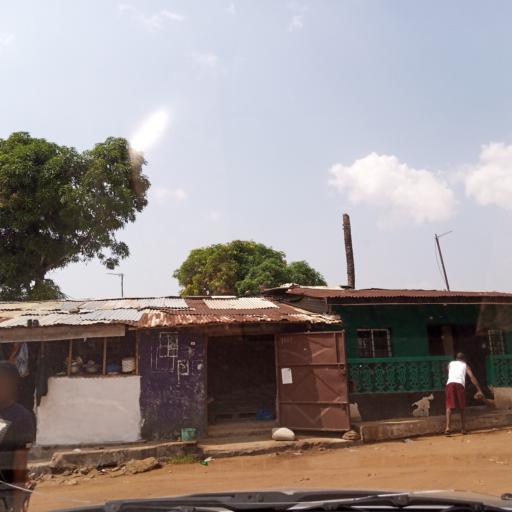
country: LR
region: Montserrado
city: Monrovia
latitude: 6.2905
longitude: -10.7661
